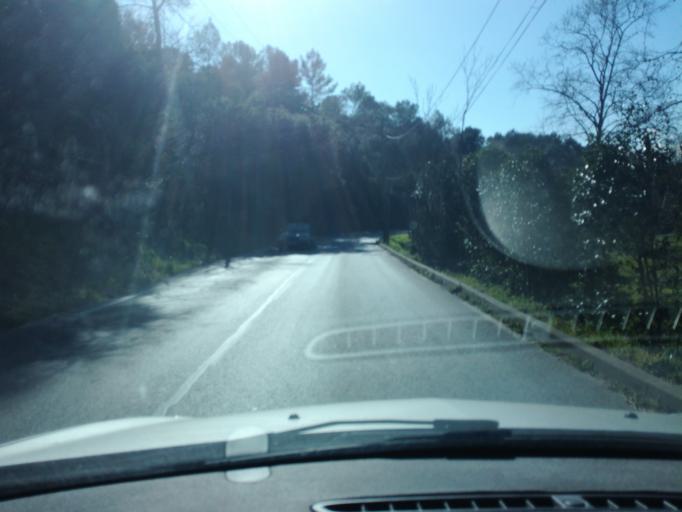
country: FR
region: Provence-Alpes-Cote d'Azur
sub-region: Departement des Alpes-Maritimes
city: Pegomas
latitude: 43.6322
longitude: 6.9310
